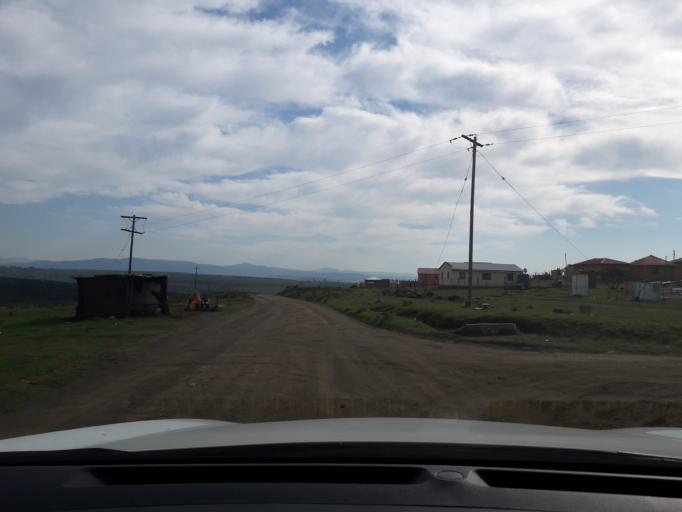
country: ZA
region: Eastern Cape
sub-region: Buffalo City Metropolitan Municipality
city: Bhisho
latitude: -32.9333
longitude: 27.3774
